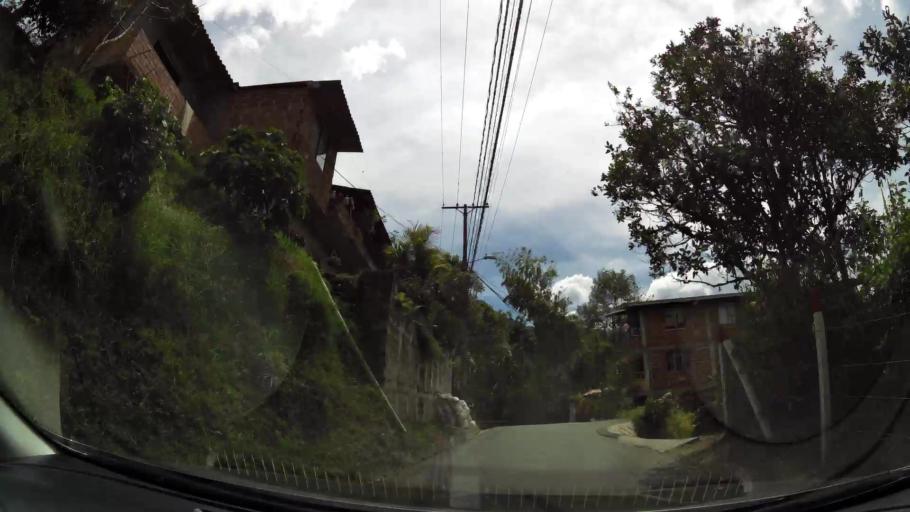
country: CO
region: Antioquia
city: Municipio de Copacabana
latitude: 6.3285
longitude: -75.5000
